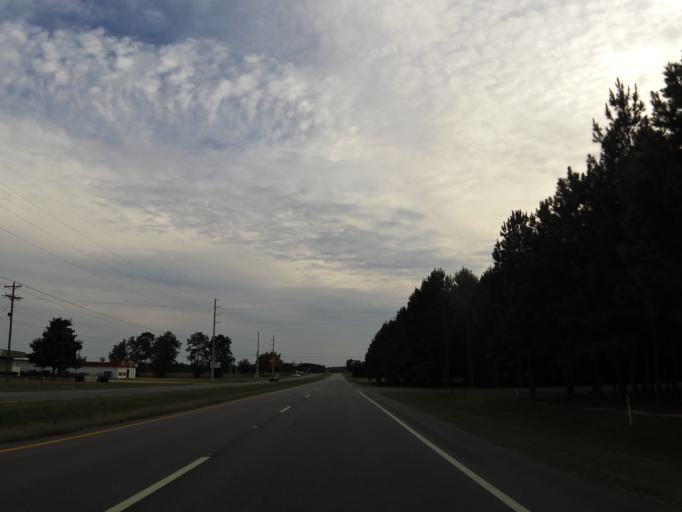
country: US
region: Alabama
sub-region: Escambia County
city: Atmore
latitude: 31.0732
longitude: -87.4855
